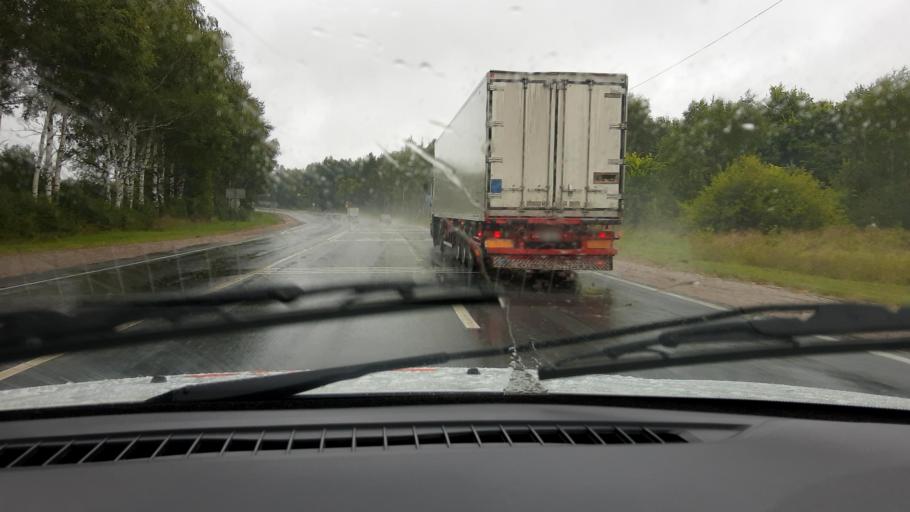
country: RU
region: Nizjnij Novgorod
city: Pamyat' Parizhskoy Kommuny
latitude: 56.0322
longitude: 44.5022
